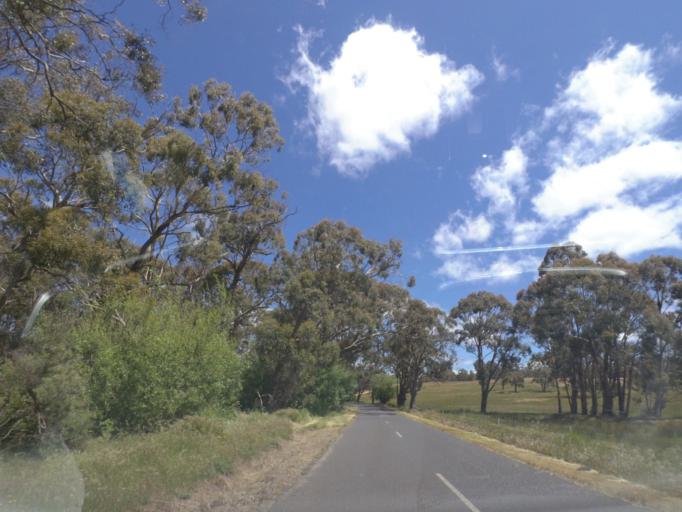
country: AU
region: Victoria
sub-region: Mount Alexander
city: Castlemaine
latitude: -37.3074
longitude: 144.1877
